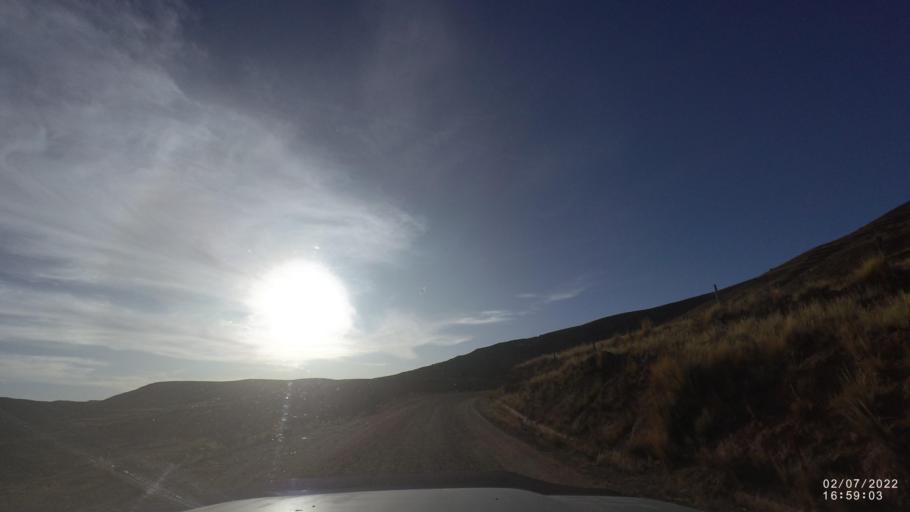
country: BO
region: Cochabamba
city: Irpa Irpa
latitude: -17.9424
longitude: -66.5497
